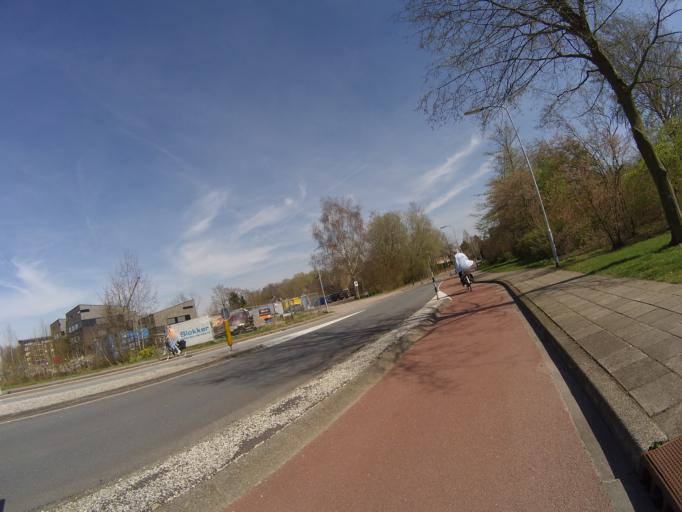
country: NL
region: Gelderland
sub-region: Gemeente Nijkerk
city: Nijkerk
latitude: 52.2287
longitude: 5.4918
